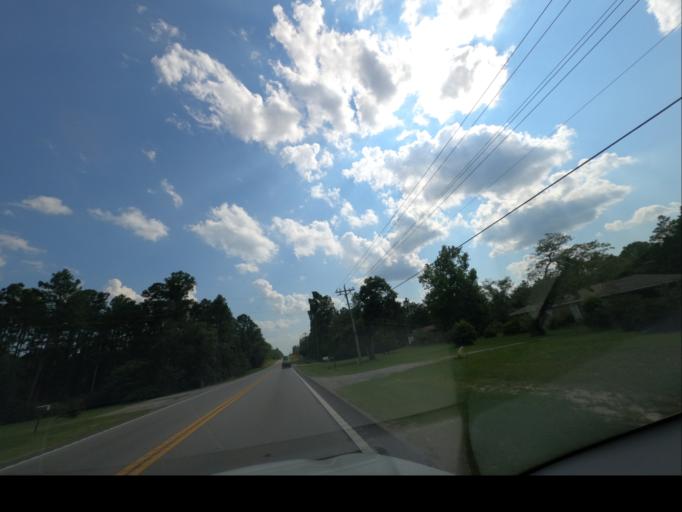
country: US
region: South Carolina
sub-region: Lexington County
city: Red Bank
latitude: 33.8485
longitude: -81.2080
